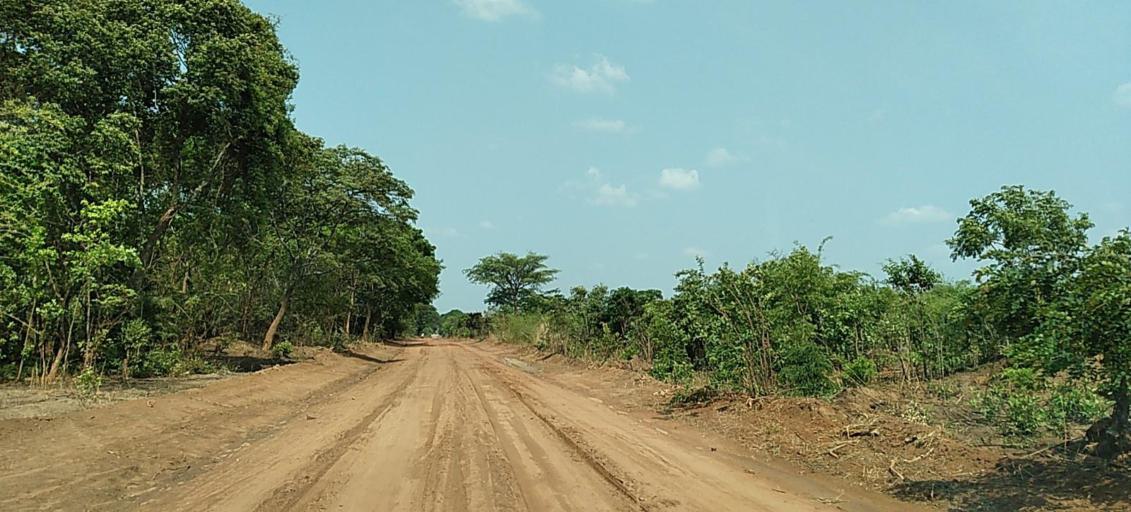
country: ZM
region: Copperbelt
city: Luanshya
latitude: -13.0905
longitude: 28.2785
